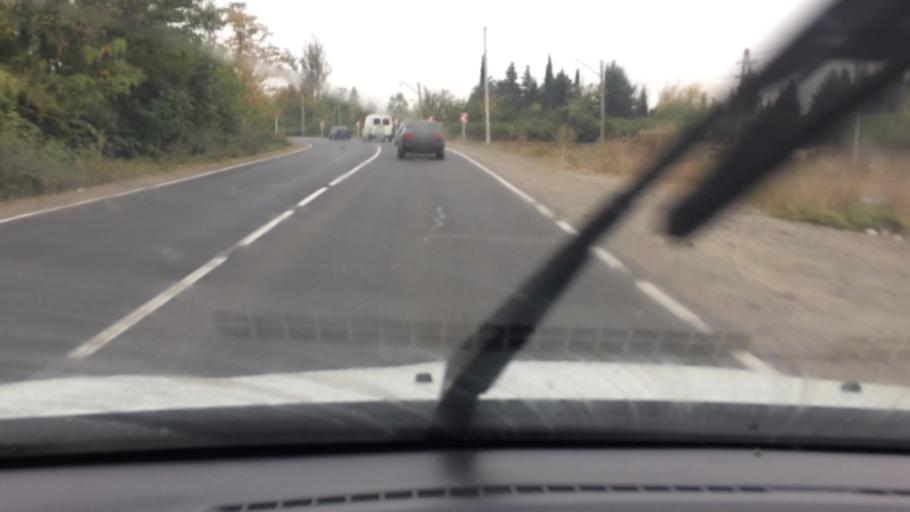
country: GE
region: Kvemo Kartli
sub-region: Marneuli
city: Marneuli
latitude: 41.4089
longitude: 44.8314
